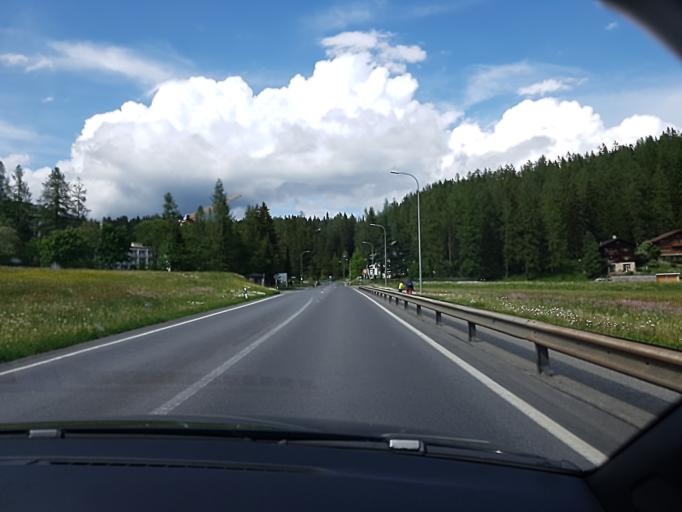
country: CH
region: Grisons
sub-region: Praettigau/Davos District
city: Davos
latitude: 46.8270
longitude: 9.8557
